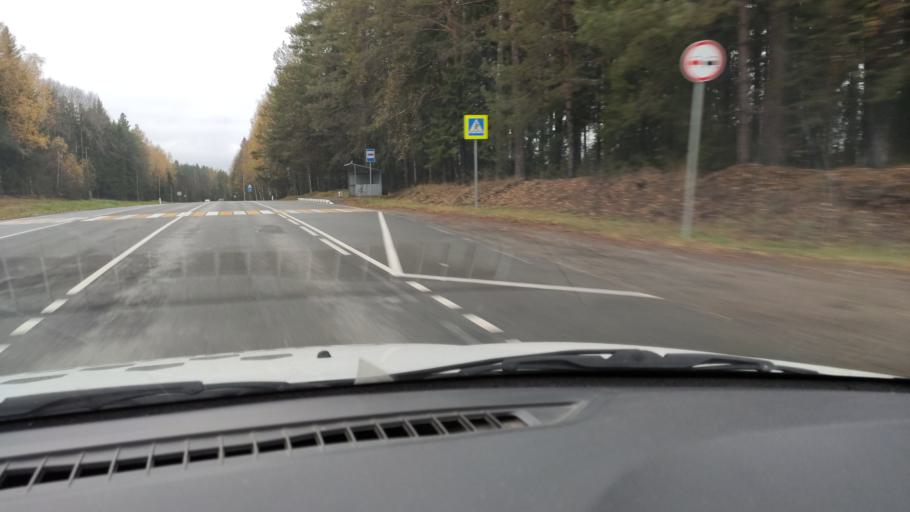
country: RU
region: Kirov
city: Belaya Kholunitsa
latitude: 58.9042
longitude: 50.9547
